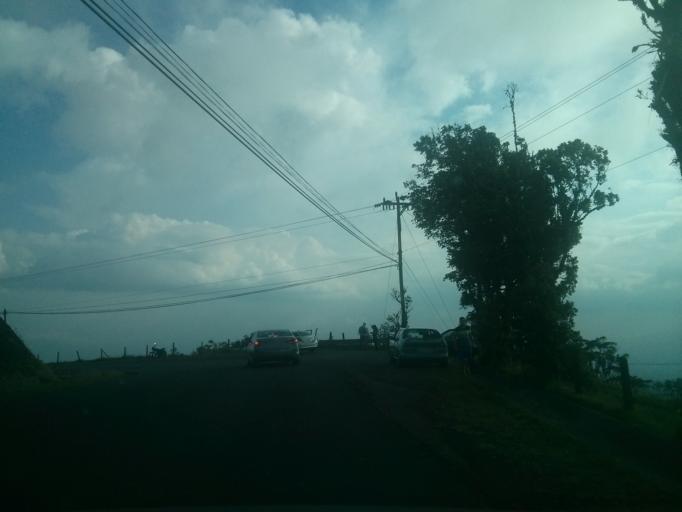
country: CR
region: Heredia
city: Santo Domingo
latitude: 10.1373
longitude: -84.1638
